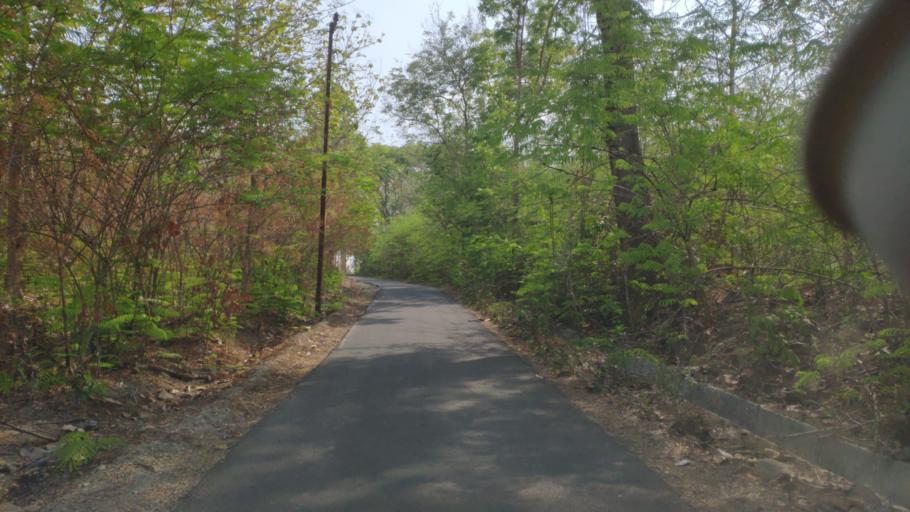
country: ID
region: Central Java
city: Randublatung
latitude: -7.2338
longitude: 111.2863
